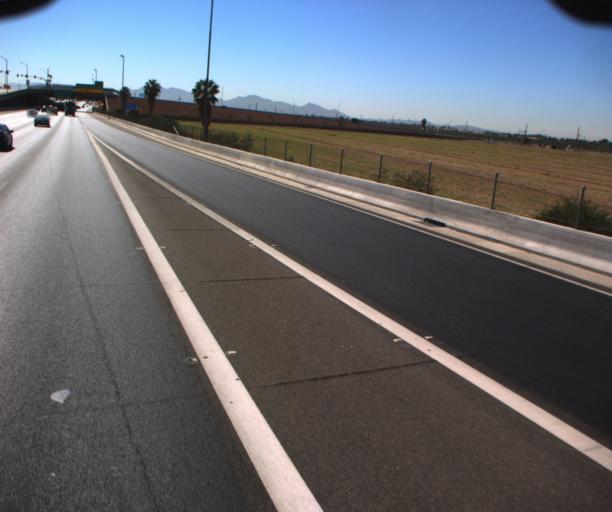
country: US
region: Arizona
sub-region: Maricopa County
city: Peoria
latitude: 33.5327
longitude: -112.2698
